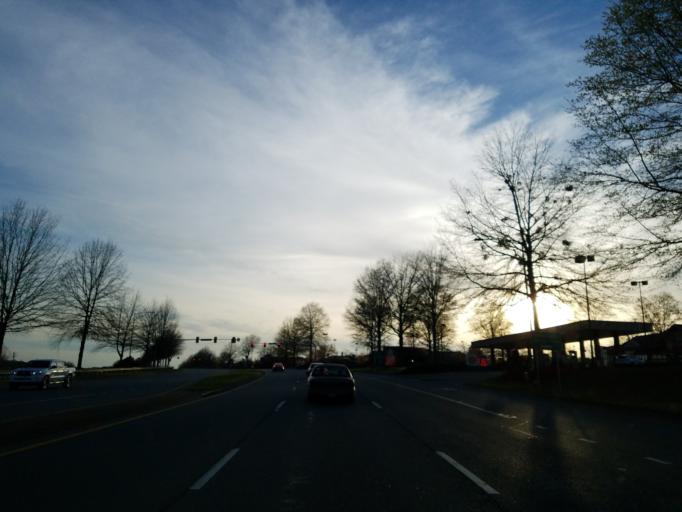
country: US
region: Georgia
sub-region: Cherokee County
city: Canton
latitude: 34.2521
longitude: -84.4719
